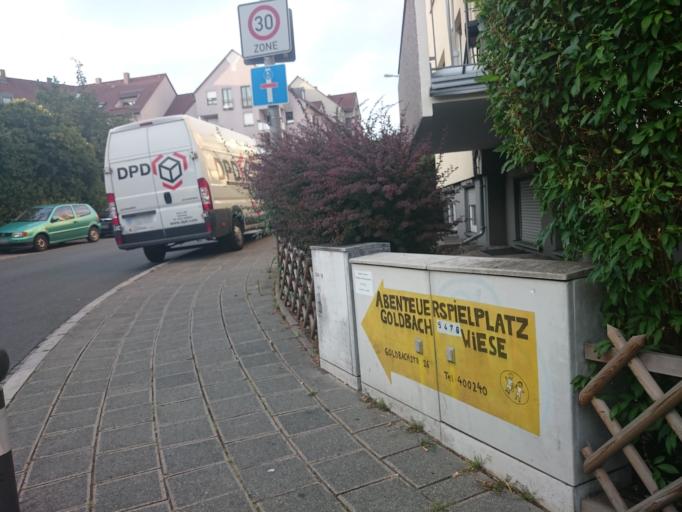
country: DE
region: Bavaria
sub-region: Regierungsbezirk Mittelfranken
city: Nuernberg
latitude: 49.4446
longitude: 11.1117
